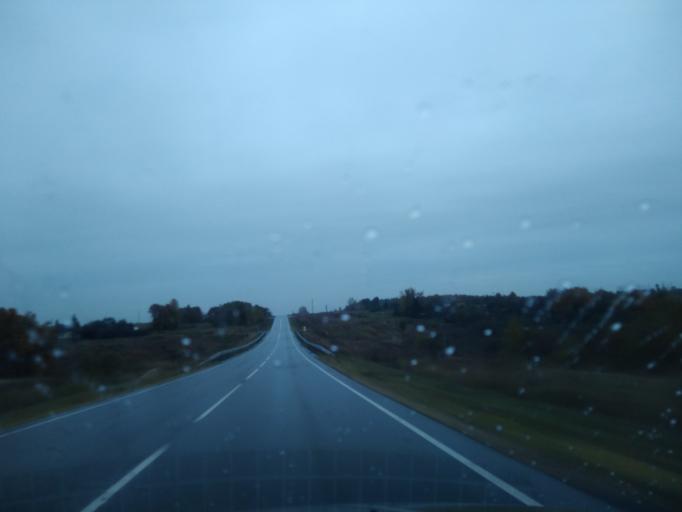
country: RU
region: Tula
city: Volovo
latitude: 53.4099
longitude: 37.8220
